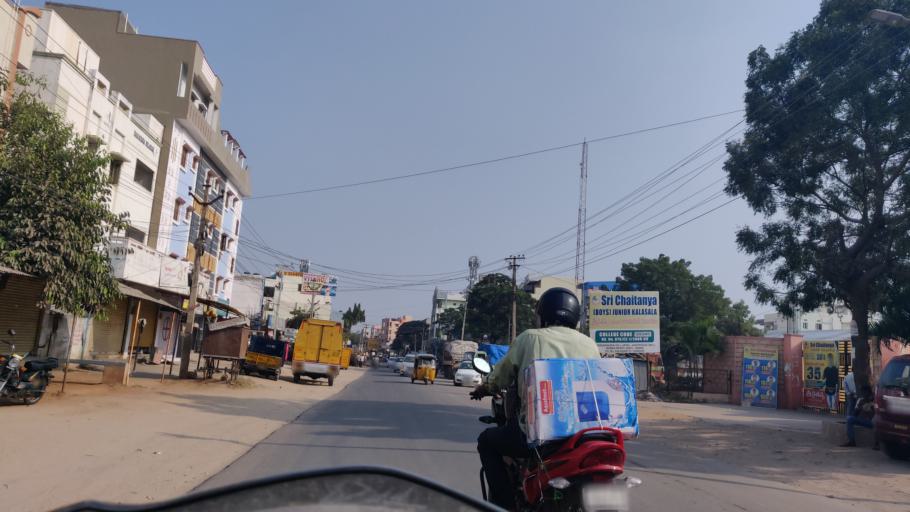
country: IN
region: Telangana
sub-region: Rangareddi
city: Uppal Kalan
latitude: 17.3964
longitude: 78.5901
